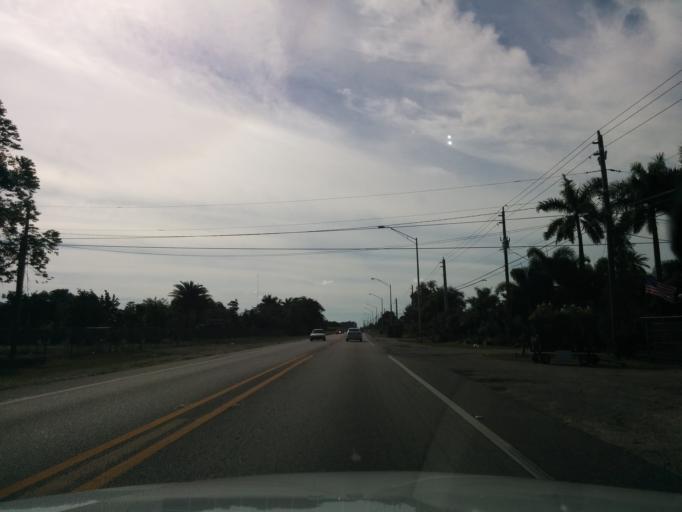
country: US
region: Florida
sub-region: Miami-Dade County
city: Richmond West
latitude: 25.5912
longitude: -80.4784
